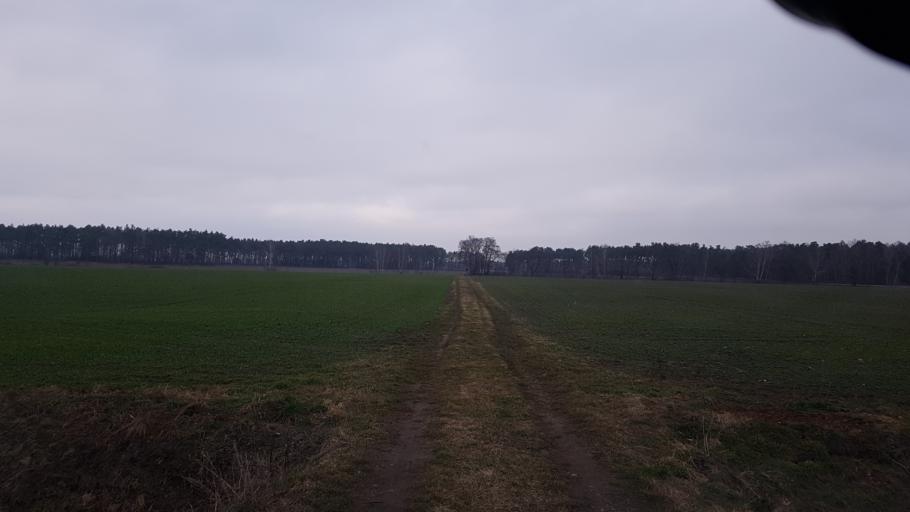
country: DE
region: Brandenburg
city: Schonewalde
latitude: 51.6400
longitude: 13.6173
